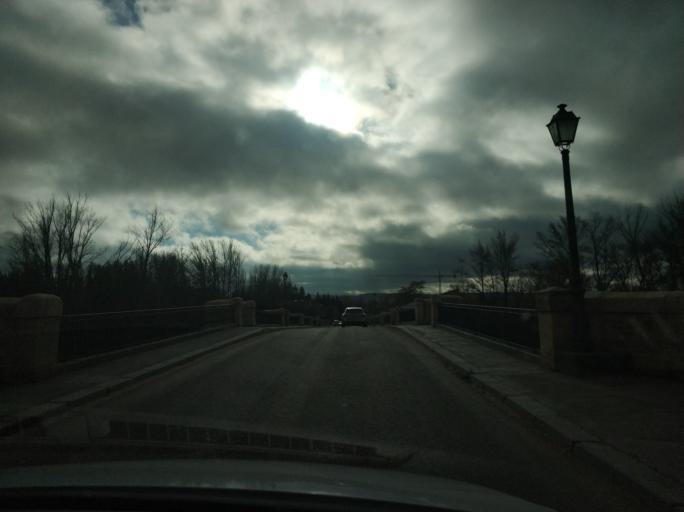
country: ES
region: Castille and Leon
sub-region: Provincia de Soria
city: San Esteban de Gormaz
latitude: 41.5728
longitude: -3.2054
